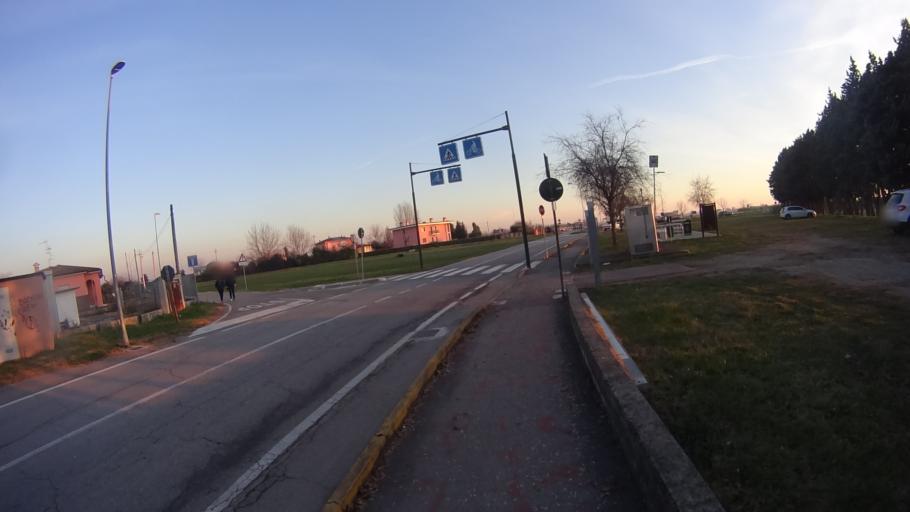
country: IT
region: Veneto
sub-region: Provincia di Verona
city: Povegliano Veronese
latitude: 45.3422
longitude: 10.8870
